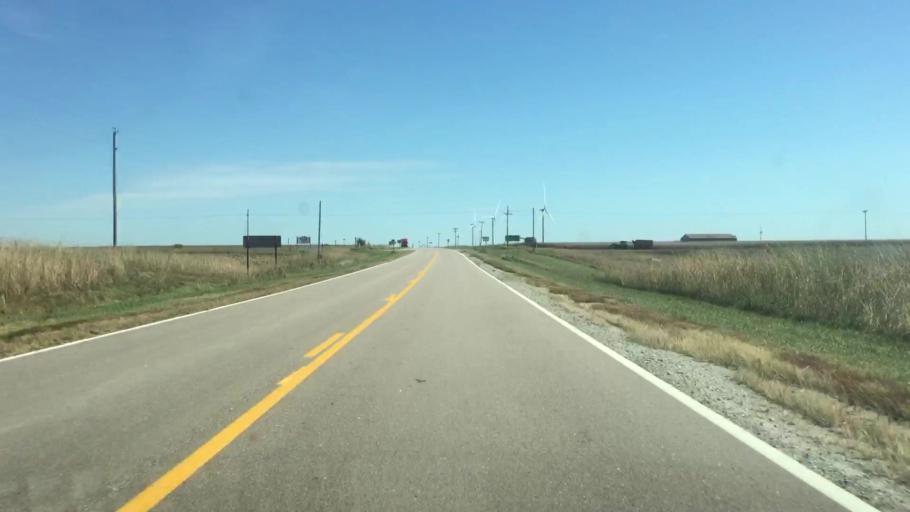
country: US
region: Kansas
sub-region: Washington County
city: Washington
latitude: 40.0448
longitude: -96.9374
